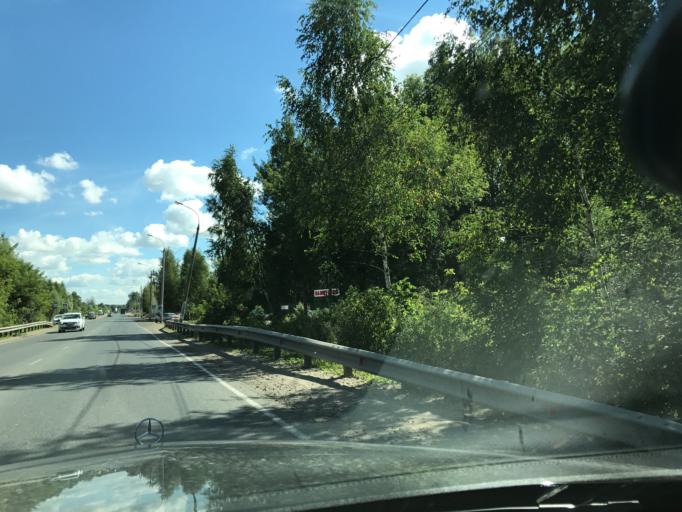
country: RU
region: Nizjnij Novgorod
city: Gorbatovka
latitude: 56.2149
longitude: 43.7598
